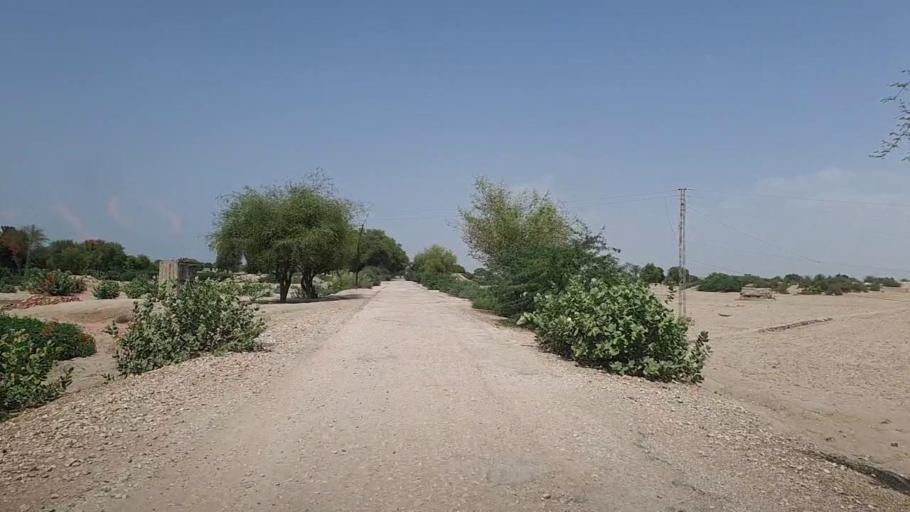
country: PK
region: Sindh
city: Pad Idan
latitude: 26.7910
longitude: 68.3530
